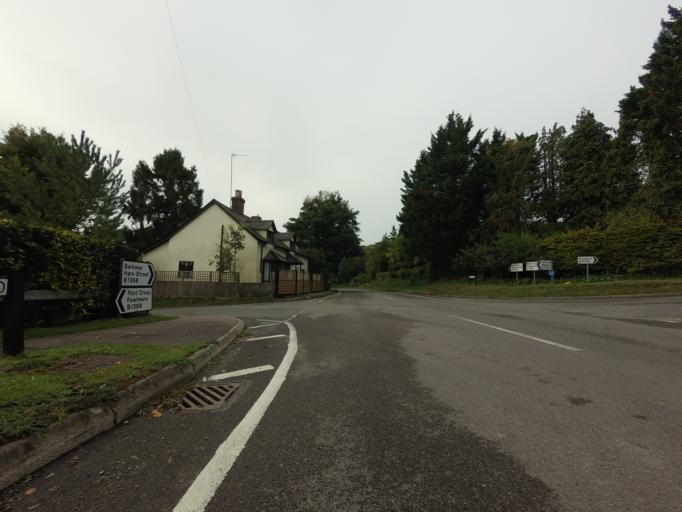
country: GB
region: England
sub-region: Cambridgeshire
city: Melbourn
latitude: 52.0319
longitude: 0.0398
